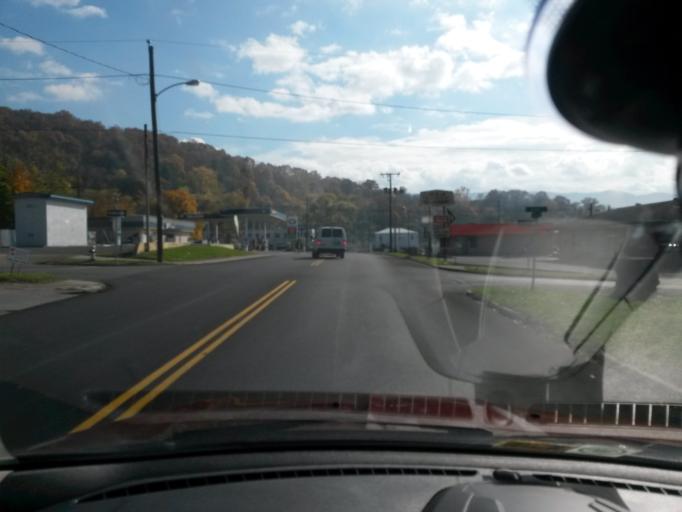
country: US
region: Virginia
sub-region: City of Covington
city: Fairlawn
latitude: 37.7846
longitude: -79.9870
